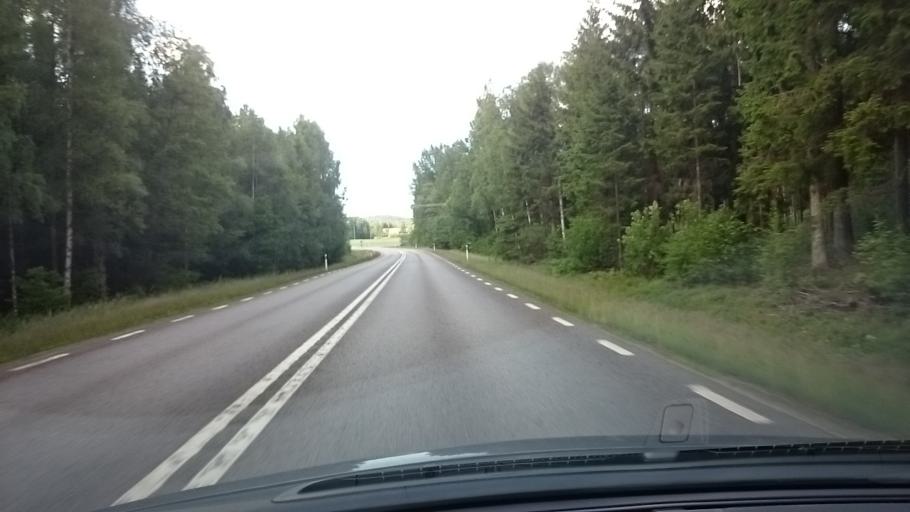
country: SE
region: OErebro
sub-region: Askersunds Kommun
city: Askersund
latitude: 58.7616
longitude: 14.7953
